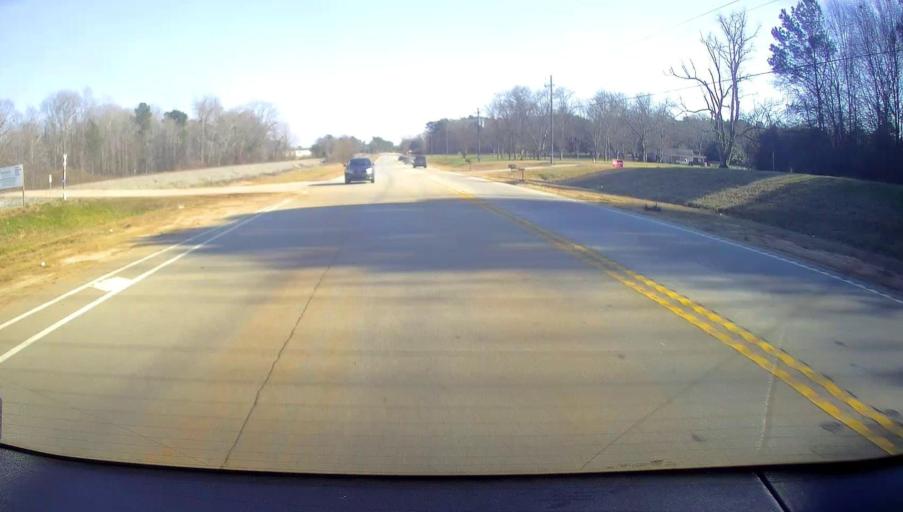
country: US
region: Georgia
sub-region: Butts County
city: Jackson
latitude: 33.3222
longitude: -83.9953
